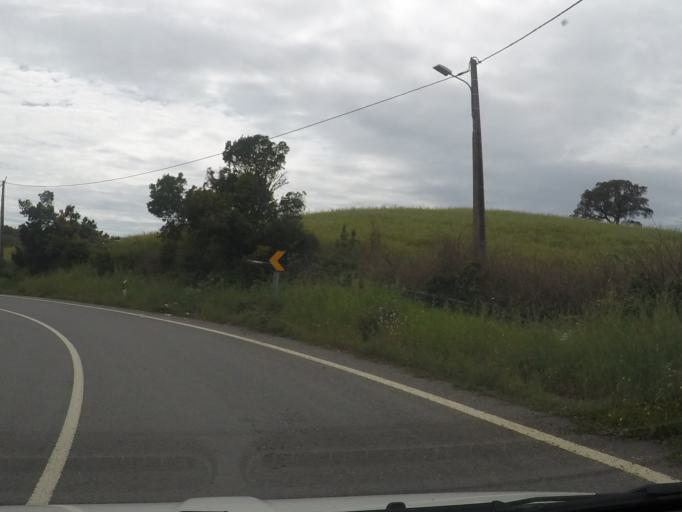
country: PT
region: Setubal
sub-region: Sines
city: Porto Covo
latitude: 37.8677
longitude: -8.7262
